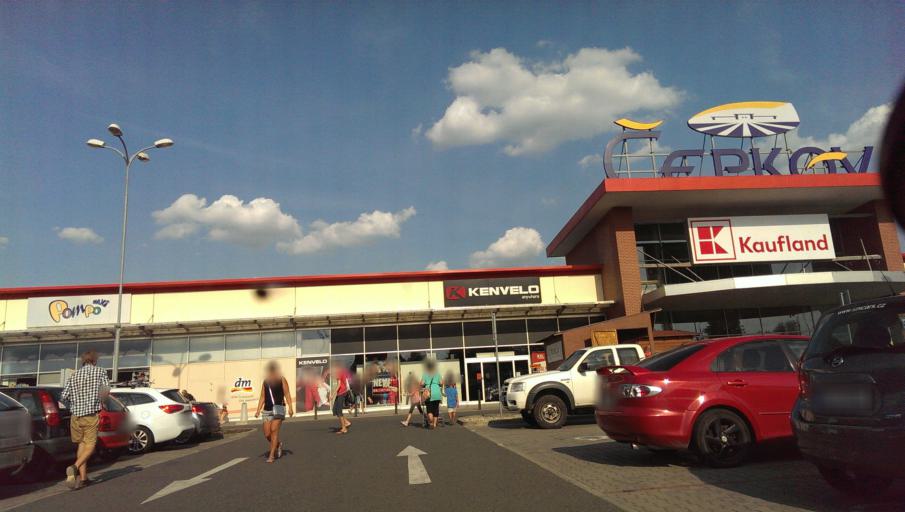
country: CZ
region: Zlin
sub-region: Okres Zlin
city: Zlin
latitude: 49.2289
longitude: 17.6610
